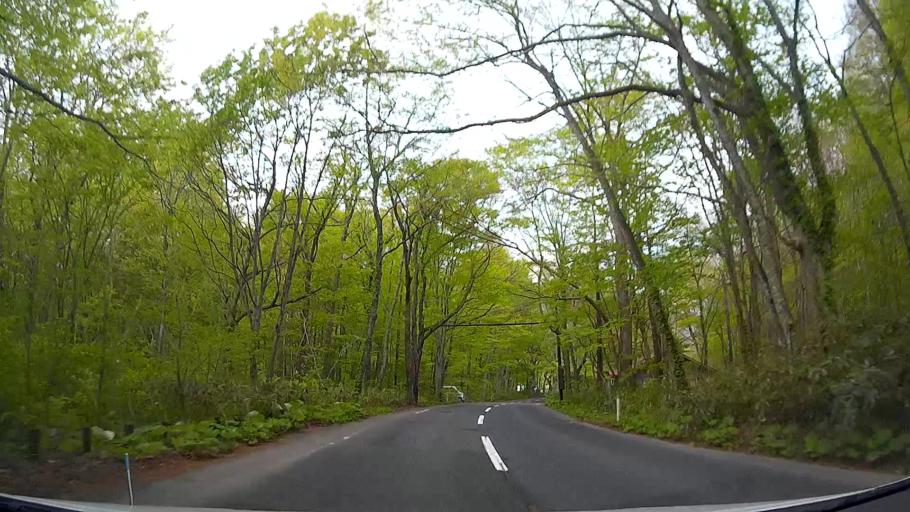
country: JP
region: Aomori
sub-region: Aomori Shi
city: Furudate
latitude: 40.5731
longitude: 140.9784
